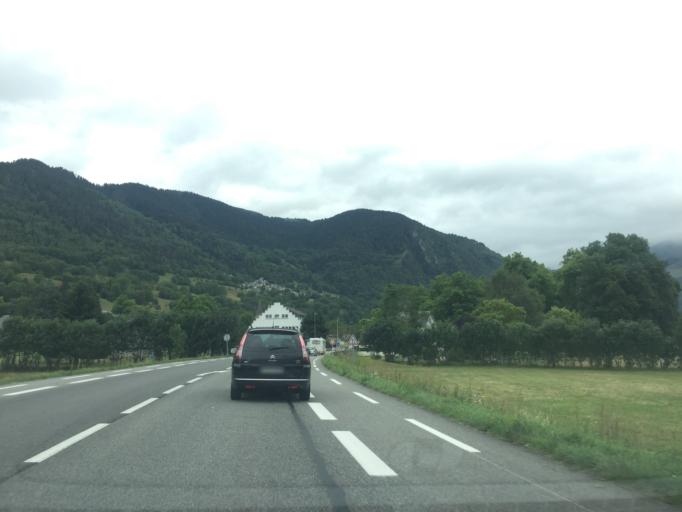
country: FR
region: Midi-Pyrenees
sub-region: Departement des Hautes-Pyrenees
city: Saint-Lary-Soulan
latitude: 42.8516
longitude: 0.3461
